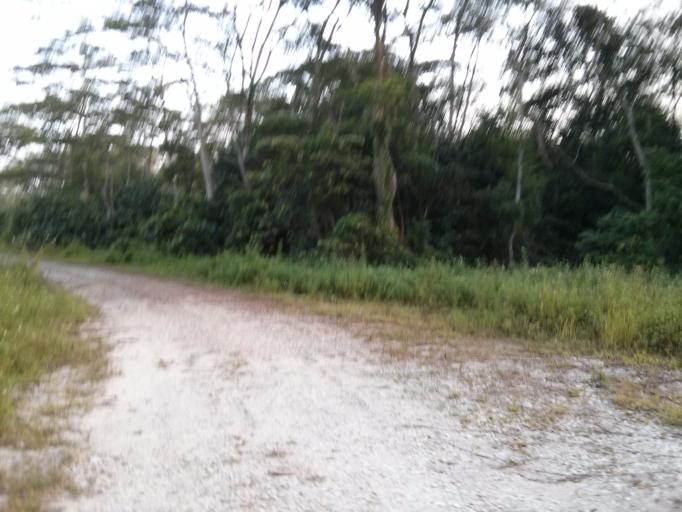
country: MY
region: Johor
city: Johor Bahru
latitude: 1.3743
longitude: 103.7336
